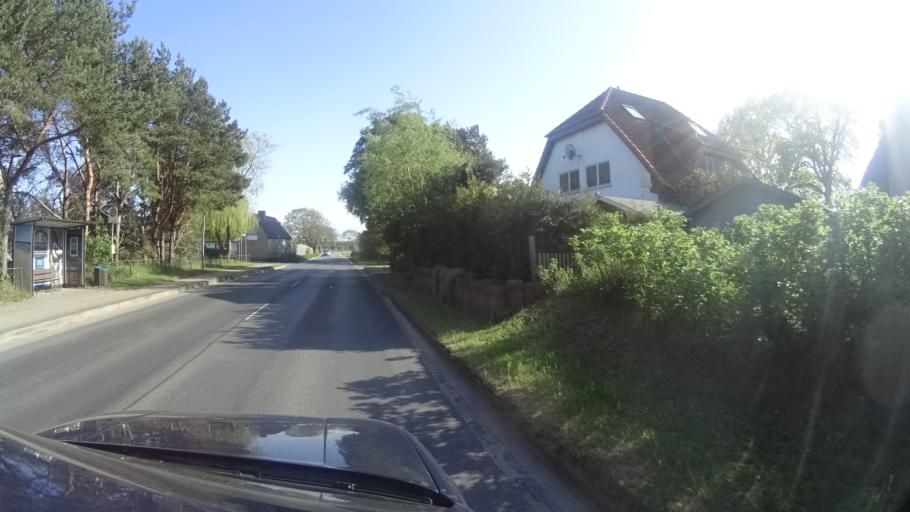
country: DE
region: Mecklenburg-Vorpommern
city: Ostseebad Prerow
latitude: 54.4078
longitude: 12.5704
